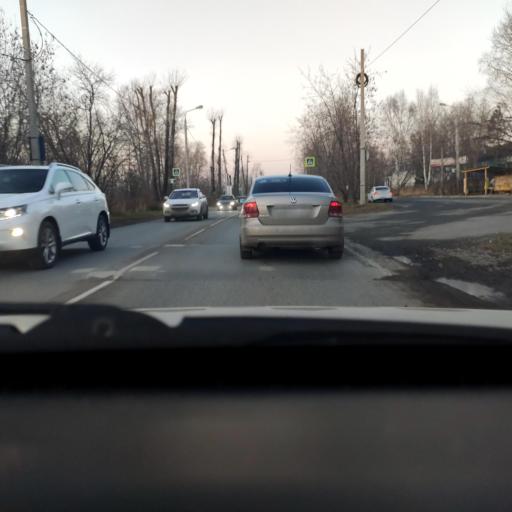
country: RU
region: Perm
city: Kondratovo
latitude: 57.9668
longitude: 56.1278
